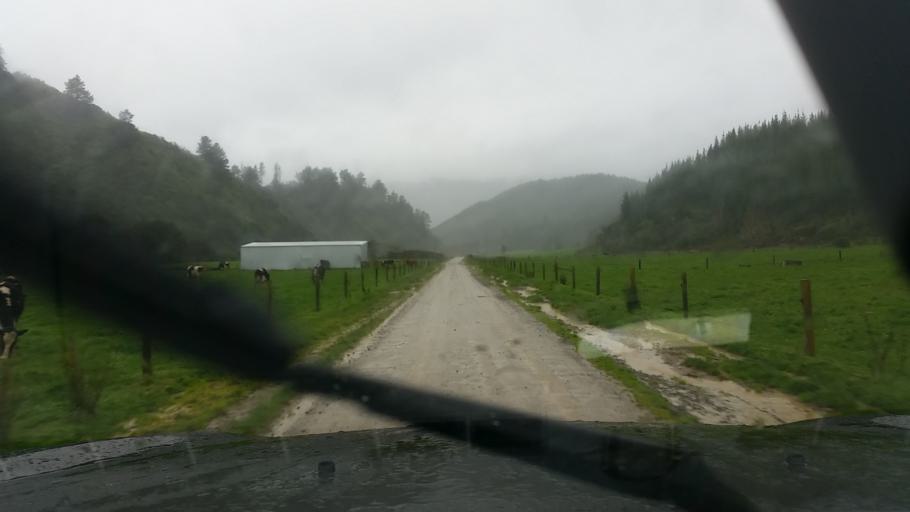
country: NZ
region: Marlborough
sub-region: Marlborough District
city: Picton
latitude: -41.3518
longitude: 173.9173
